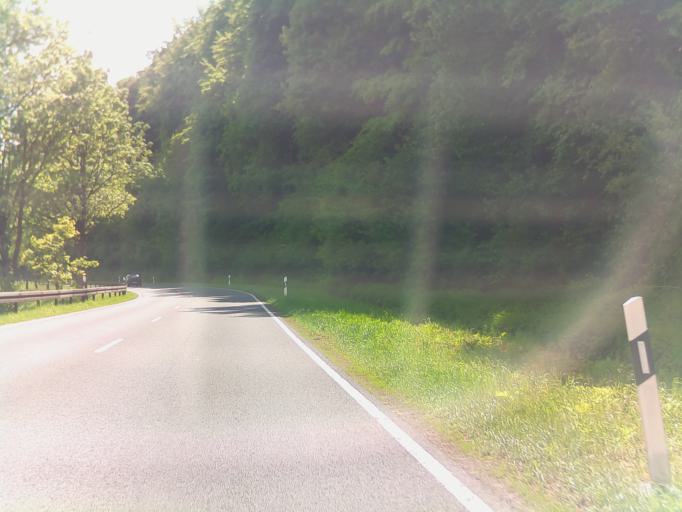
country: DE
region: Thuringia
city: Belrieth
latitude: 50.5268
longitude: 10.5097
